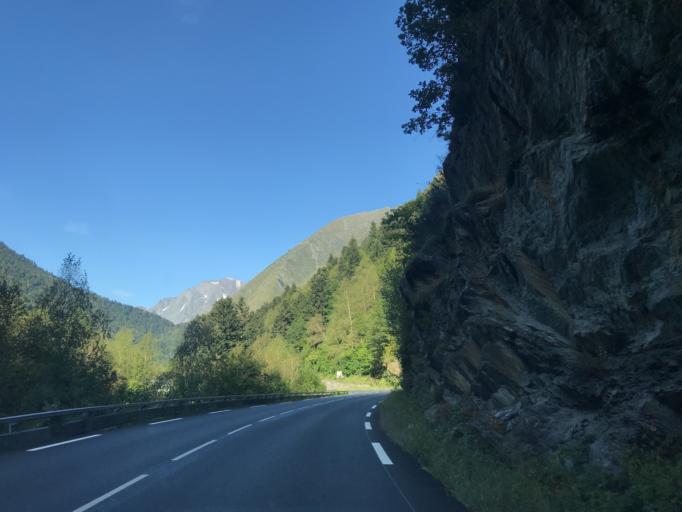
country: FR
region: Midi-Pyrenees
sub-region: Departement des Hautes-Pyrenees
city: Saint-Lary-Soulan
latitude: 42.7870
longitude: 0.2531
